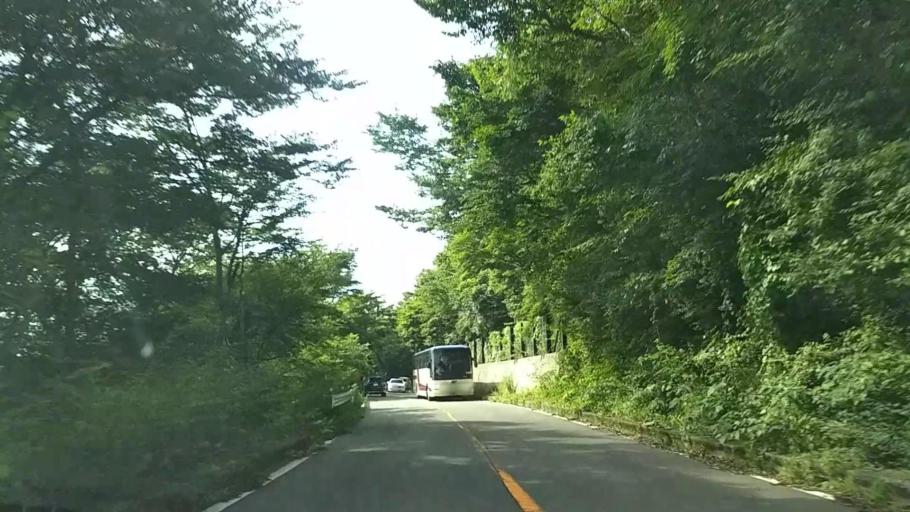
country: JP
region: Kanagawa
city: Hakone
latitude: 35.2280
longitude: 139.0002
